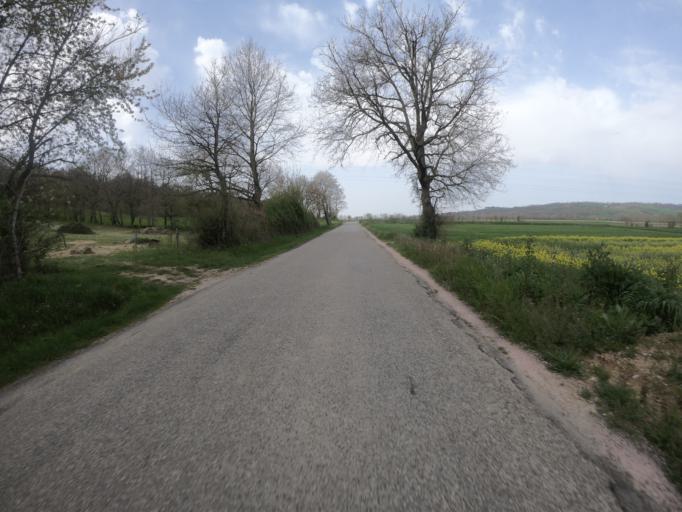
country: FR
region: Midi-Pyrenees
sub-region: Departement de l'Ariege
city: La Tour-du-Crieu
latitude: 43.1229
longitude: 1.7208
